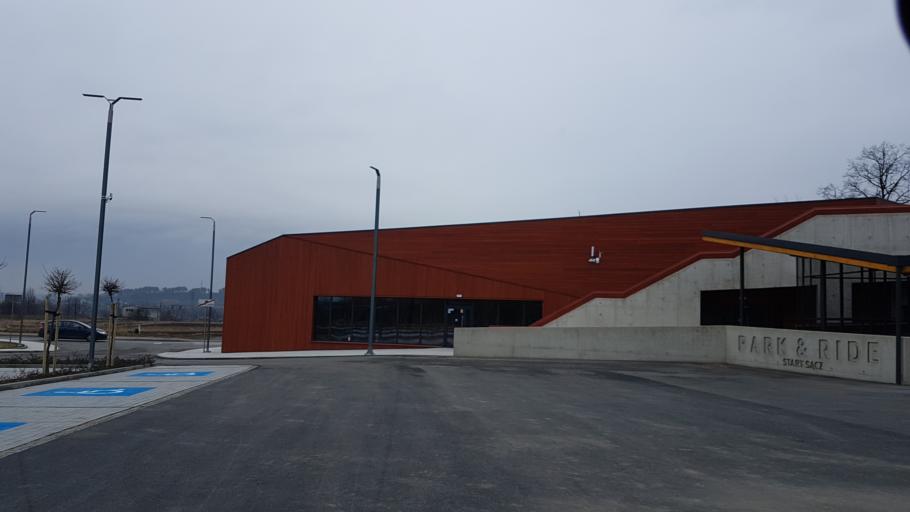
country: PL
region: Lesser Poland Voivodeship
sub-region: Powiat nowosadecki
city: Stary Sacz
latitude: 49.5657
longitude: 20.6389
